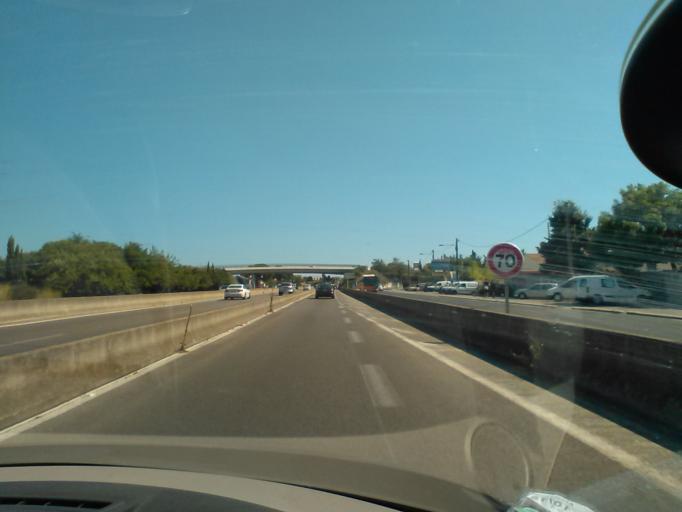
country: FR
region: Languedoc-Roussillon
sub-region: Departement de l'Herault
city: Perols
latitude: 43.5560
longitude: 3.9656
